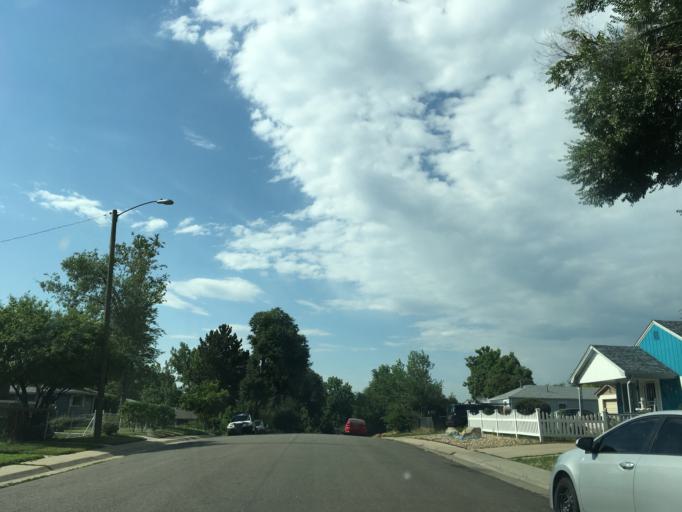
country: US
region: Colorado
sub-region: Jefferson County
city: Lakewood
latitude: 39.6980
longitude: -105.0379
